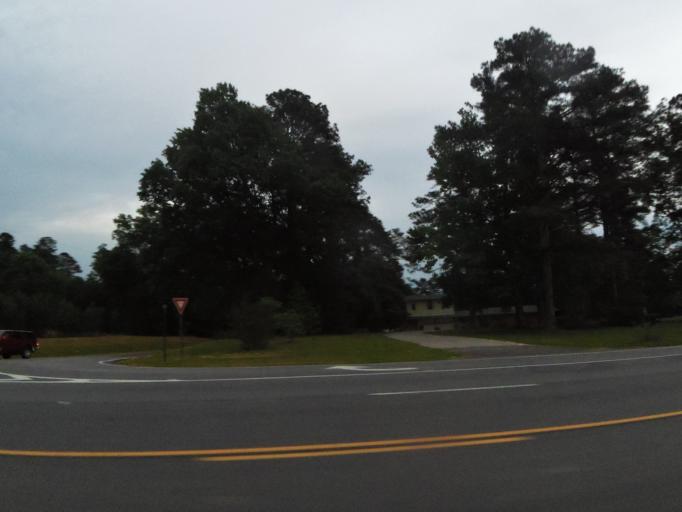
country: US
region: Georgia
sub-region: McDuffie County
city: Thomson
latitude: 33.5403
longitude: -82.5081
